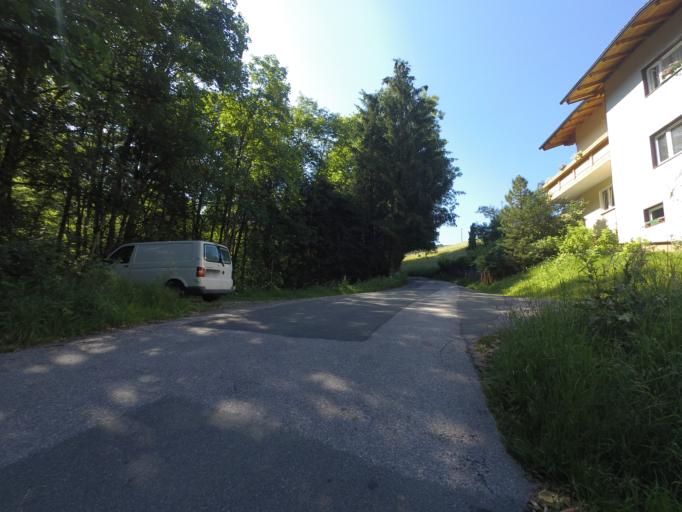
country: AT
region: Salzburg
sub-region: Politischer Bezirk Salzburg-Umgebung
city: Elsbethen
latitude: 47.7639
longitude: 13.1039
